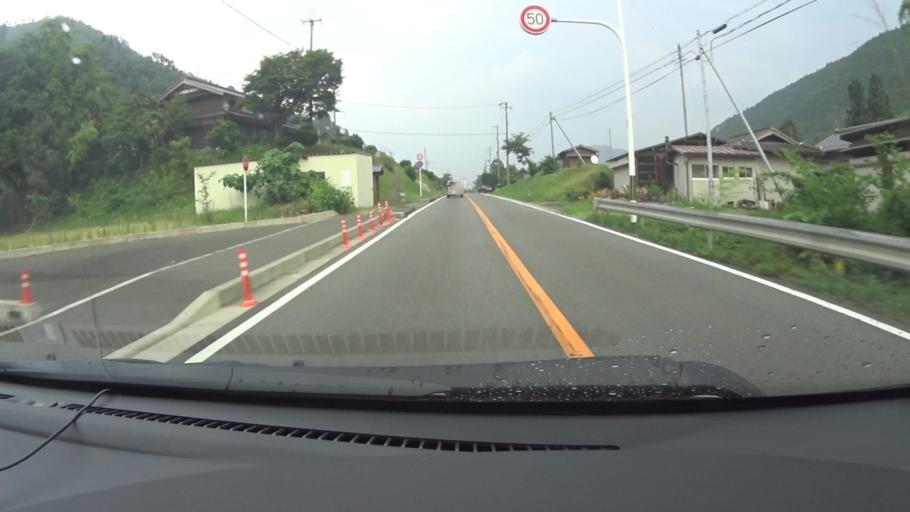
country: JP
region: Kyoto
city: Ayabe
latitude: 35.2324
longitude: 135.4140
